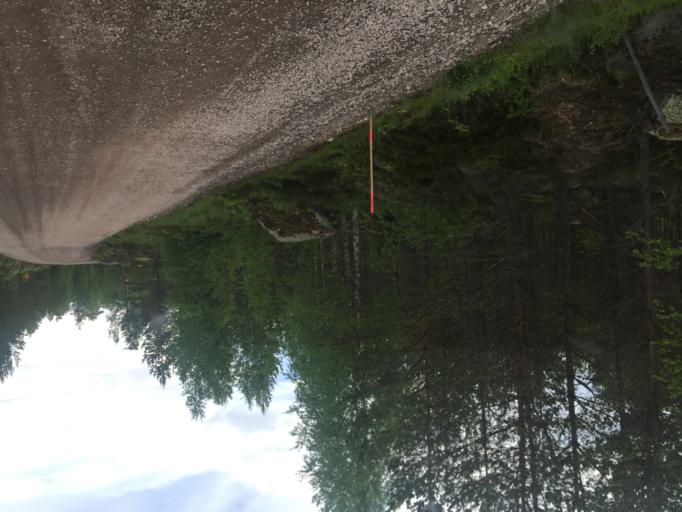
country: SE
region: Vaermland
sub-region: Hagfors Kommun
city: Hagfors
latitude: 60.2899
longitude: 13.7803
